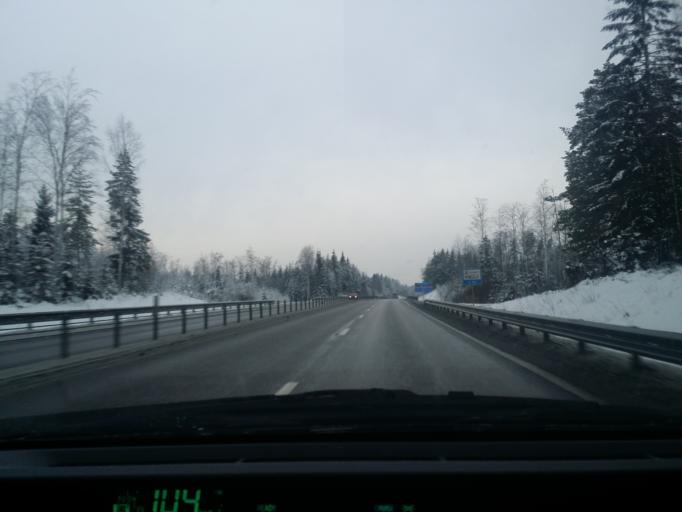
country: SE
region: Vaestra Goetaland
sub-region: Gullspangs Kommun
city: Anderstorp
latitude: 58.9111
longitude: 14.3714
